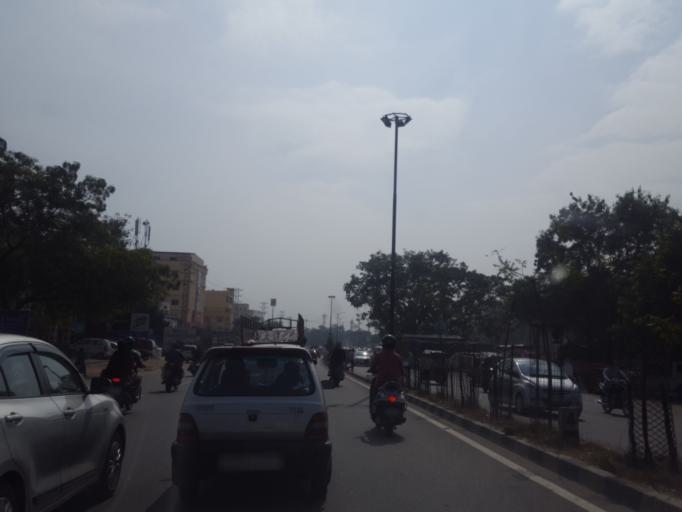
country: IN
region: Telangana
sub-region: Medak
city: Serilingampalle
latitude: 17.4994
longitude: 78.3135
